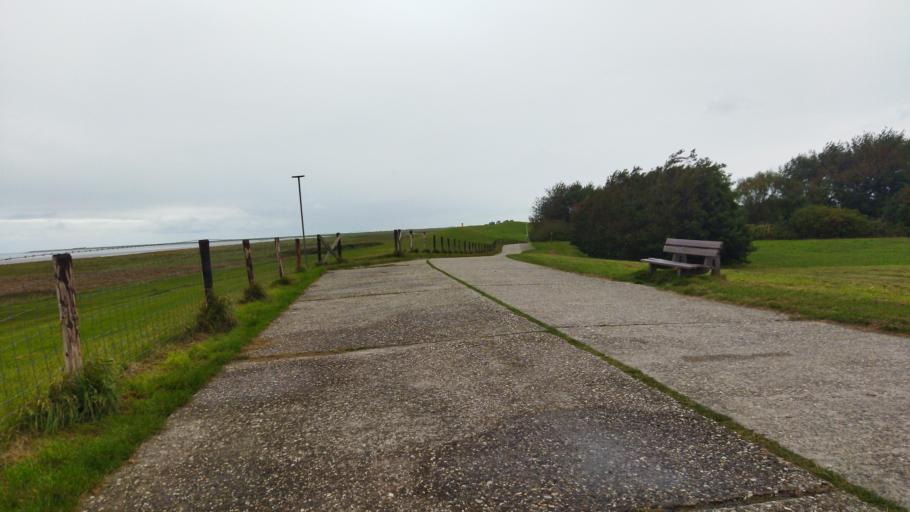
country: DE
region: Lower Saxony
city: Hinte
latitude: 53.4844
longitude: 7.0294
